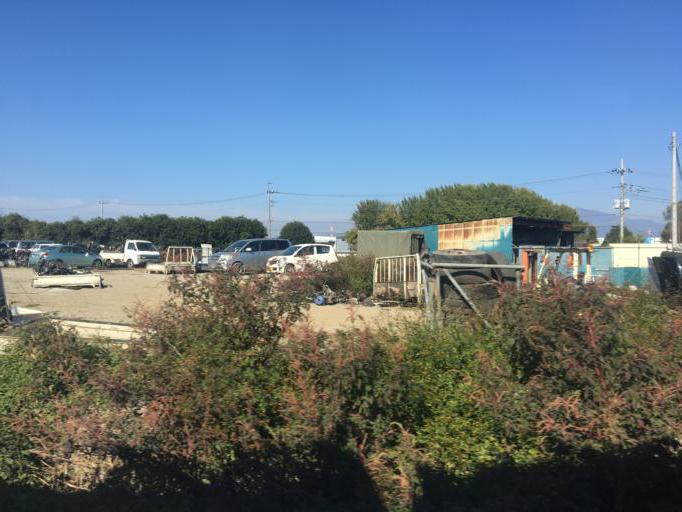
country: JP
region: Gunma
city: Omamacho-omama
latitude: 36.3721
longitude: 139.2600
